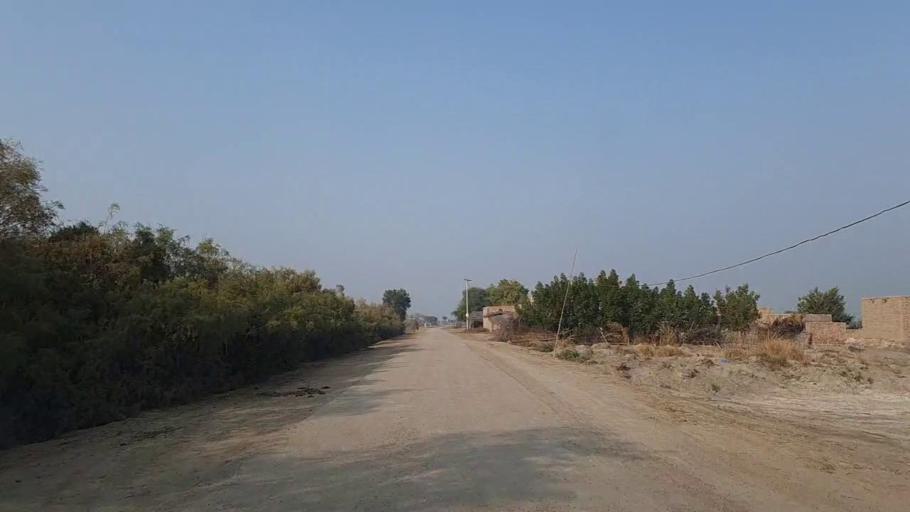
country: PK
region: Sindh
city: Nawabshah
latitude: 26.3412
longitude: 68.4892
